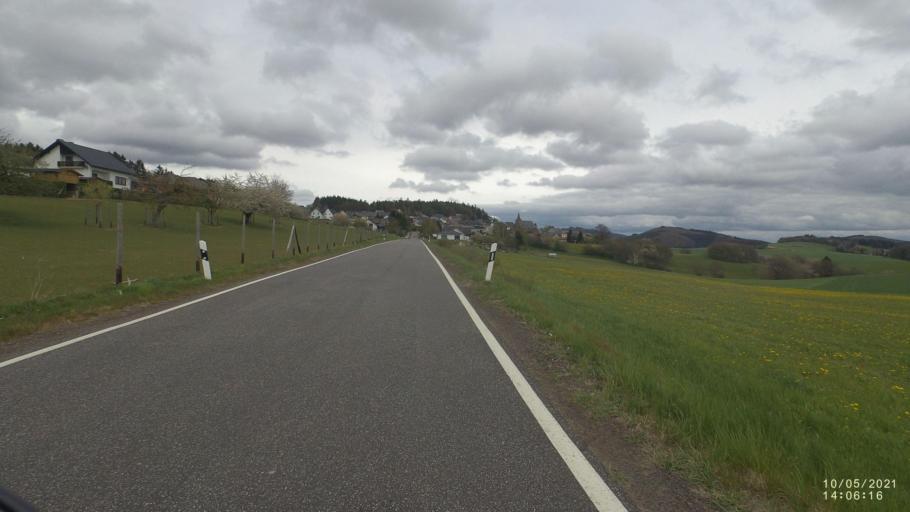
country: DE
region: Rheinland-Pfalz
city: Welschenbach
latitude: 50.3501
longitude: 7.0444
